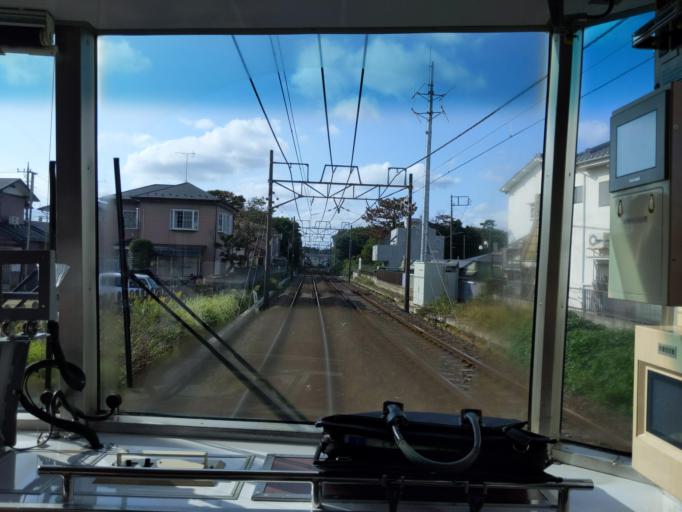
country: JP
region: Chiba
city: Shiroi
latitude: 35.7586
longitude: 140.0120
